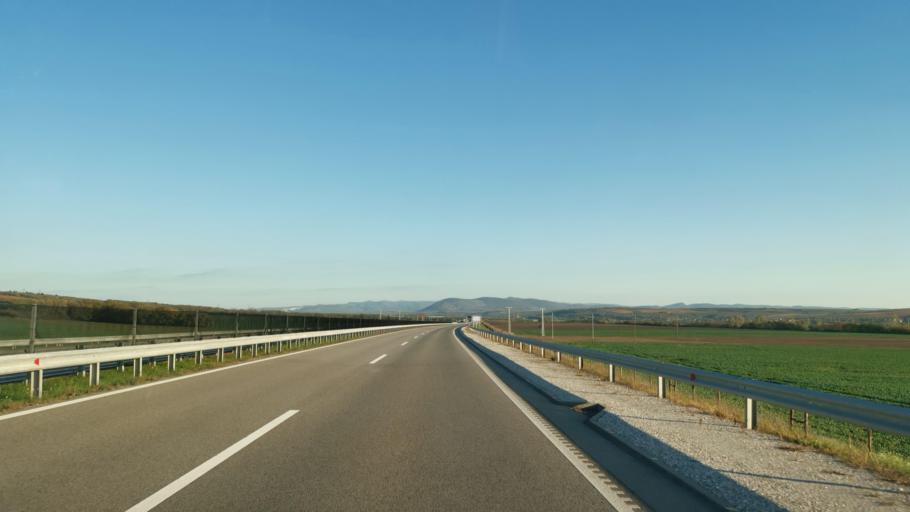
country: HU
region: Heves
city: Maklar
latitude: 47.8179
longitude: 20.3960
